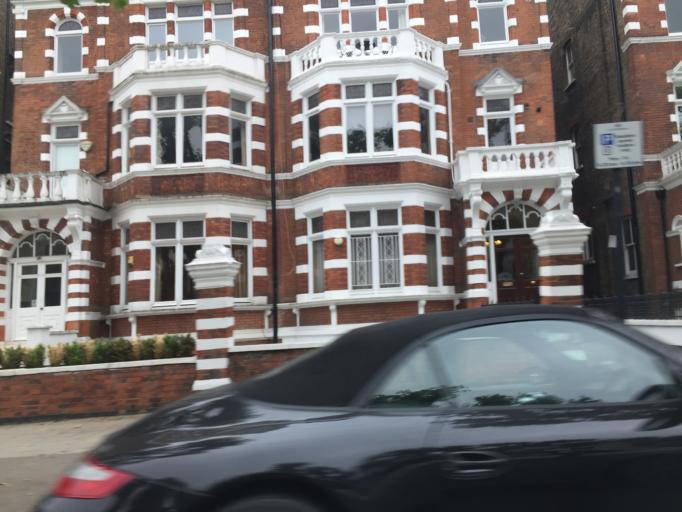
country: GB
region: England
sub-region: Greater London
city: Bayswater
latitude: 51.5294
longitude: -0.1800
